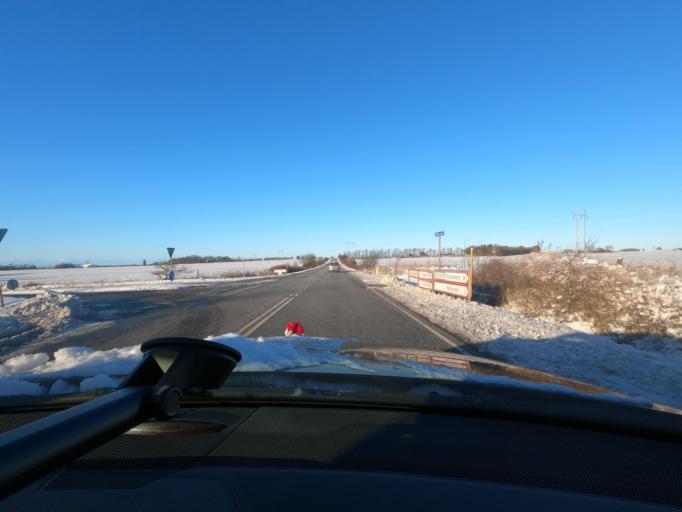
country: DK
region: South Denmark
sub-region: Aabenraa Kommune
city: Rodekro
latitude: 55.0970
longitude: 9.1923
